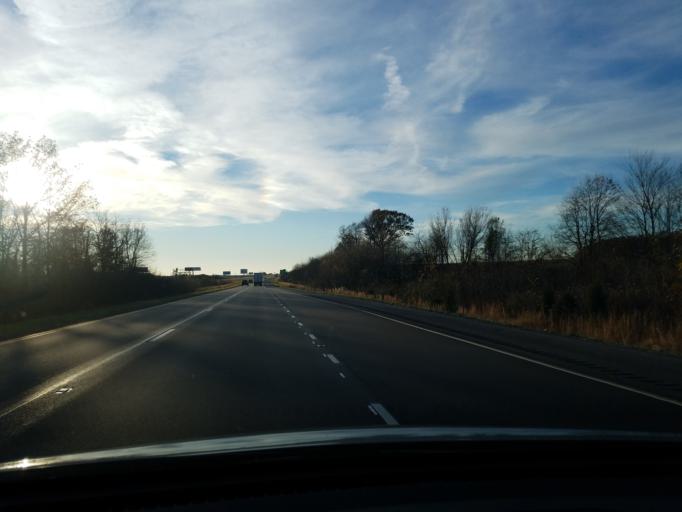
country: US
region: Indiana
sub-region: Spencer County
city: Dale
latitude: 38.1958
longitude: -86.9554
